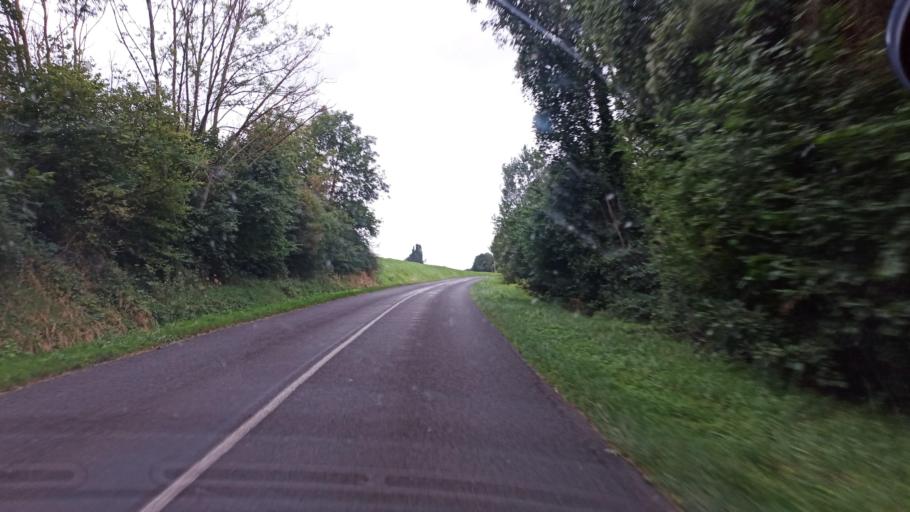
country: FR
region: Ile-de-France
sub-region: Departement de Seine-et-Marne
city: Voulx
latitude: 48.2768
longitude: 2.9834
